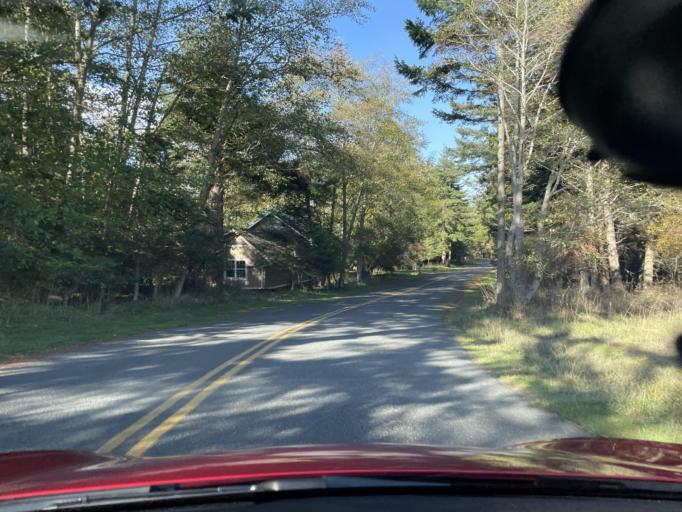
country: US
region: Washington
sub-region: San Juan County
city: Friday Harbor
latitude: 48.4577
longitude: -122.9662
